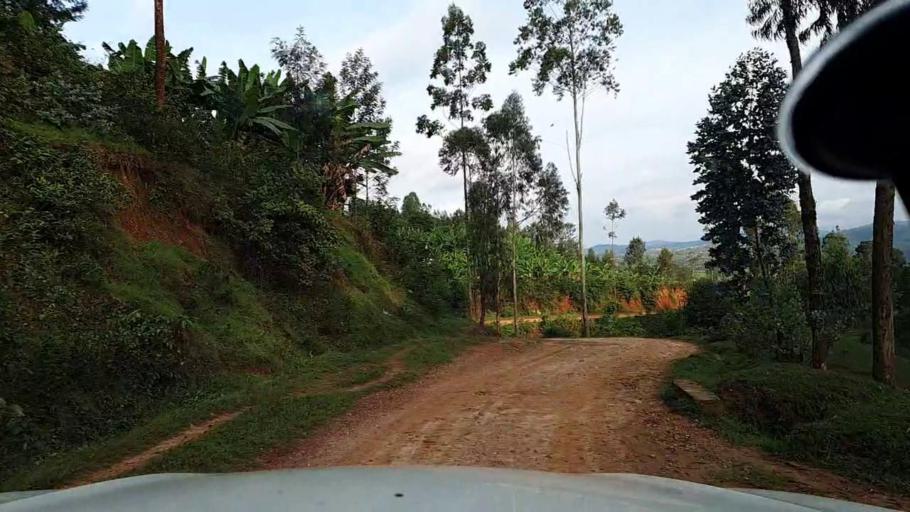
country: RW
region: Southern Province
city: Gitarama
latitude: -2.1877
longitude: 29.5734
